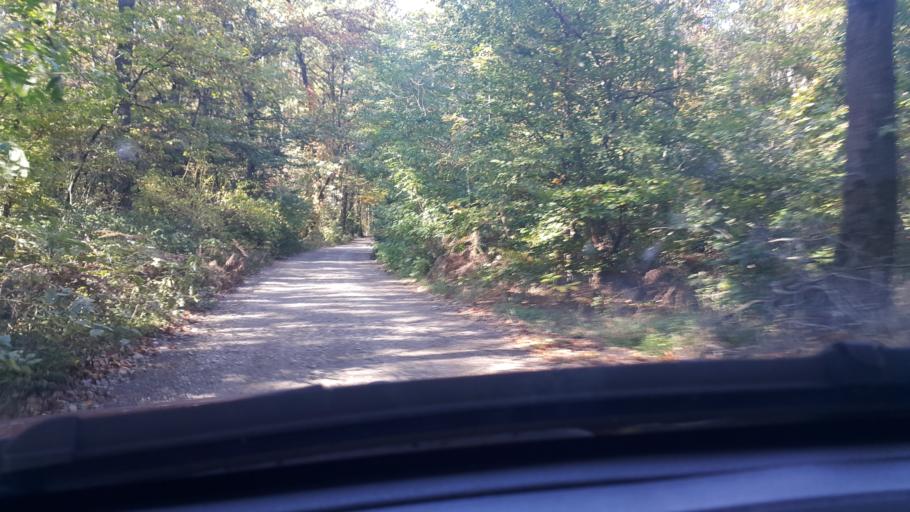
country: SI
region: Miklavz na Dravskem Polju
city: Miklavz na Dravskem Polju
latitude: 46.5359
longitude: 15.6848
